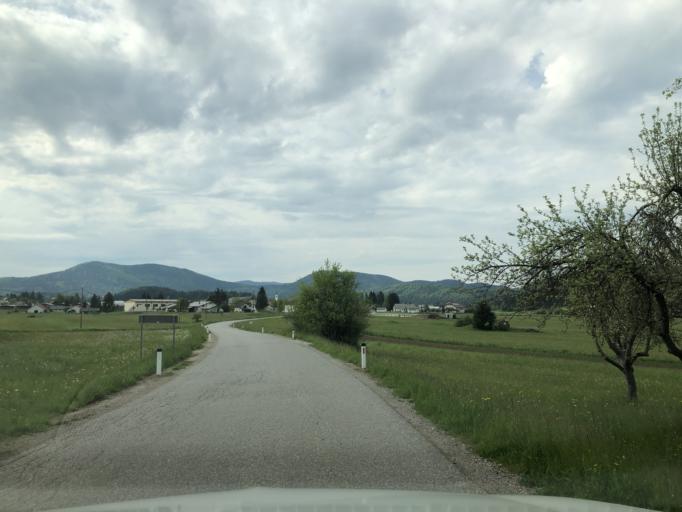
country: SI
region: Bloke
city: Nova Vas
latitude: 45.7781
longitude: 14.5041
